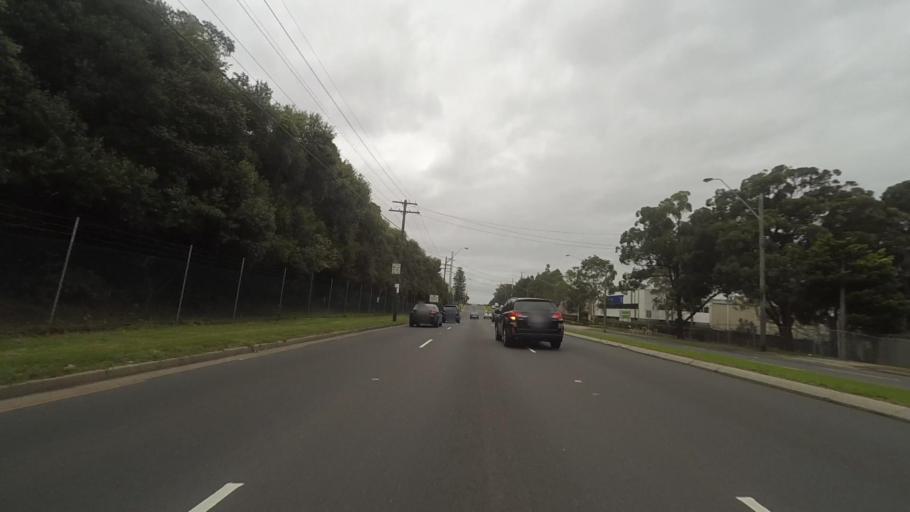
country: AU
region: New South Wales
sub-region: Auburn
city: Berala
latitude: -33.8901
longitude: 151.0390
